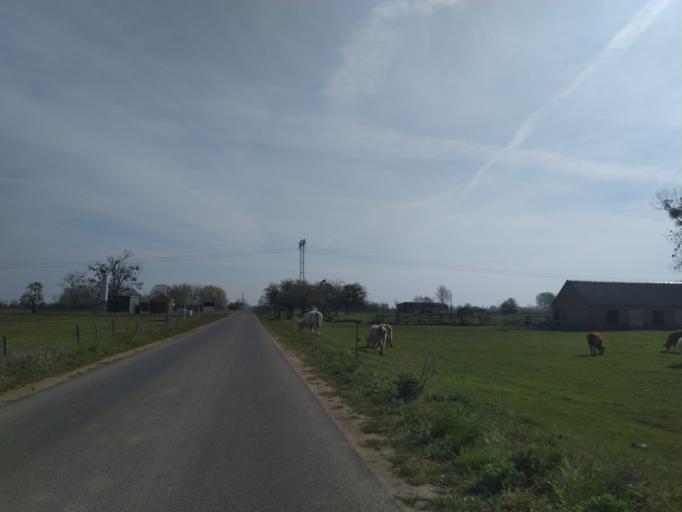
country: DE
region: Brandenburg
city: Wriezen
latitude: 52.7247
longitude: 14.1432
